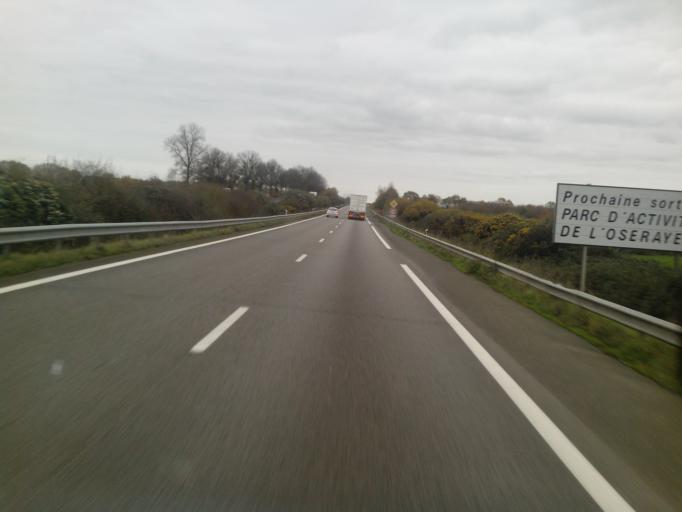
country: FR
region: Pays de la Loire
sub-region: Departement de la Loire-Atlantique
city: La Grigonnais
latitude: 47.5308
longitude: -1.6381
